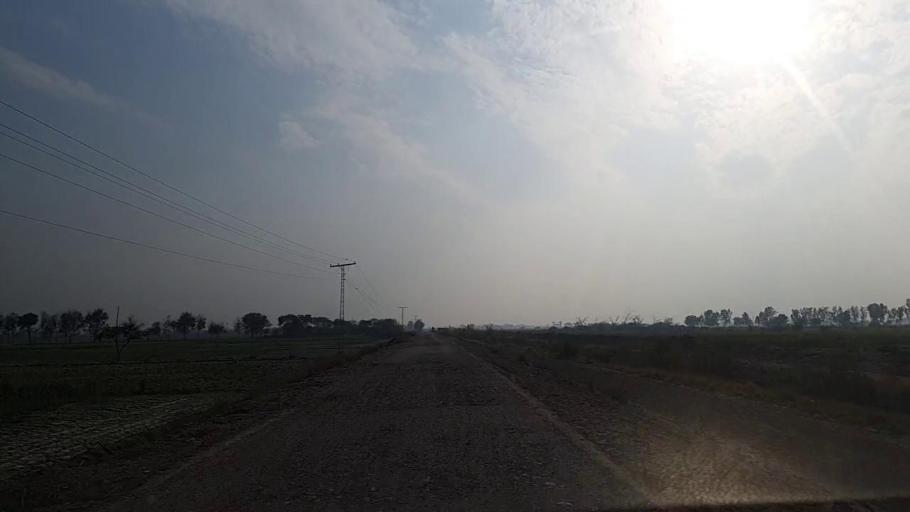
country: PK
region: Sindh
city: Jam Sahib
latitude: 26.3166
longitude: 68.5266
